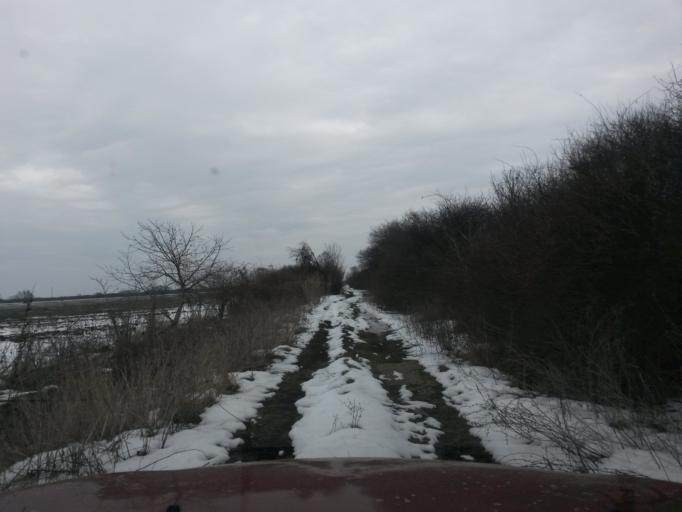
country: SK
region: Kosicky
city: Vinne
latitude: 48.7432
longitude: 22.0239
